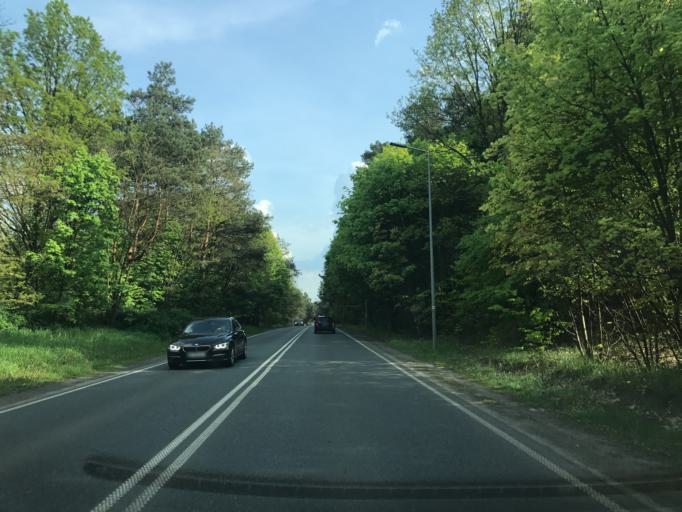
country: PL
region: Kujawsko-Pomorskie
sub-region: Bydgoszcz
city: Fordon
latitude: 53.0898
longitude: 18.1148
